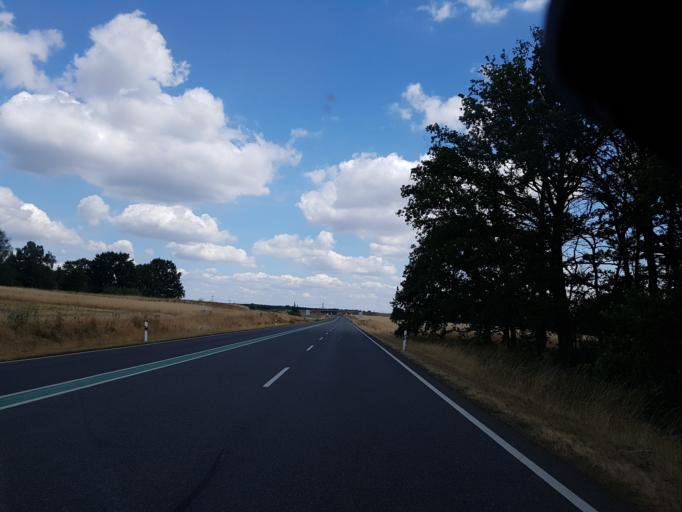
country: DE
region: Brandenburg
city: Drebkau
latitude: 51.6475
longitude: 14.2394
